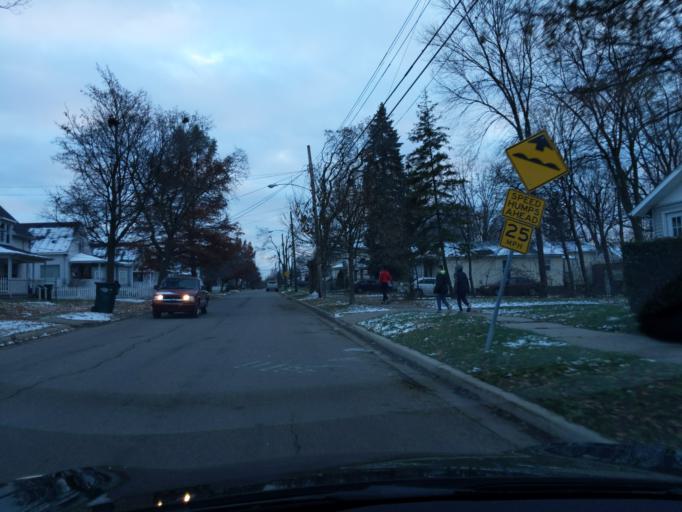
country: US
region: Michigan
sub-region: Ingham County
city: Lansing
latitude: 42.7553
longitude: -84.5371
